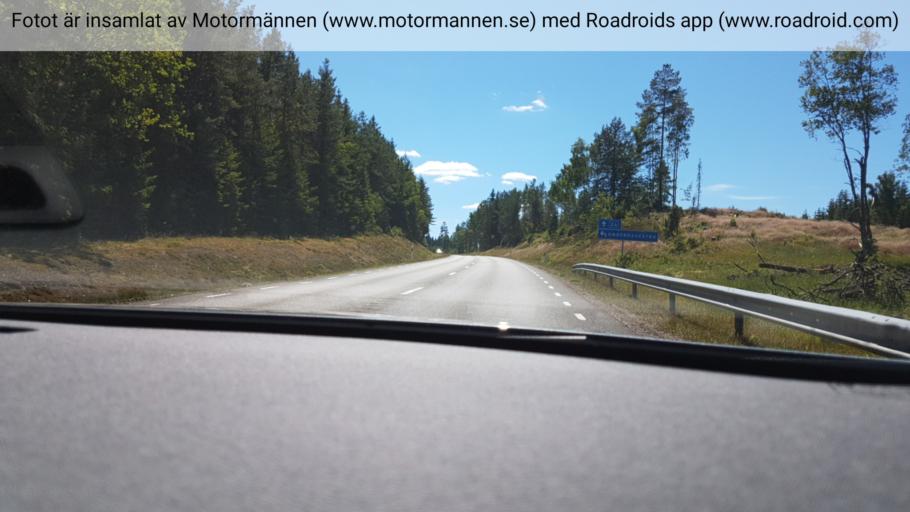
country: SE
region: Joenkoeping
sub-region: Jonkopings Kommun
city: Taberg
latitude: 57.6756
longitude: 13.8428
